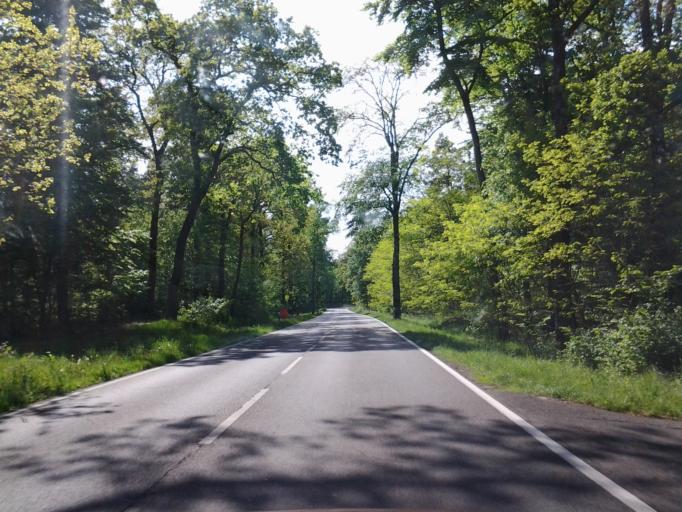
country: DE
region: Brandenburg
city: Oranienburg
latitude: 52.7642
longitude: 13.2963
